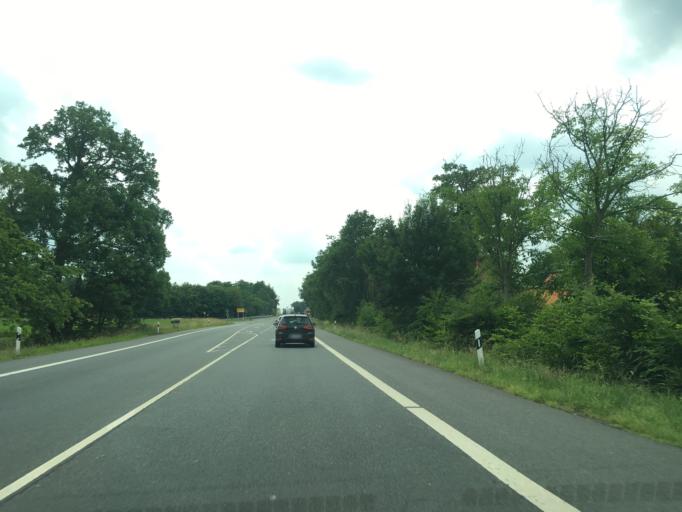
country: DE
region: North Rhine-Westphalia
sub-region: Regierungsbezirk Munster
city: Steinfurt
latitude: 52.1603
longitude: 7.3433
